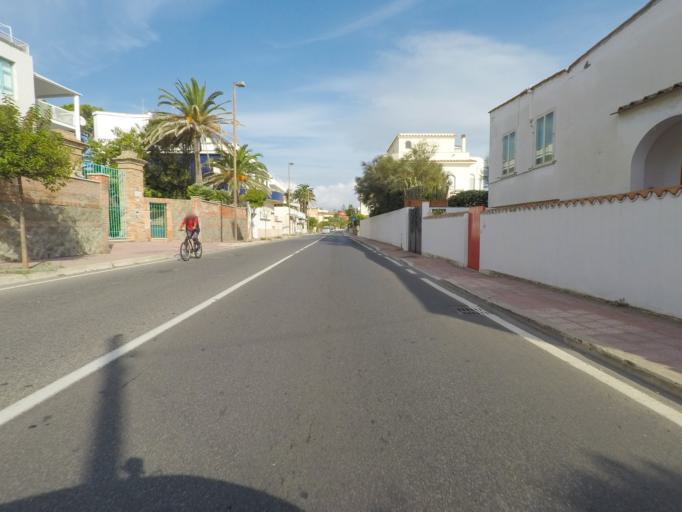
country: IT
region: Latium
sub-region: Citta metropolitana di Roma Capitale
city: Santa Marinella
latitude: 42.0339
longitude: 11.8565
